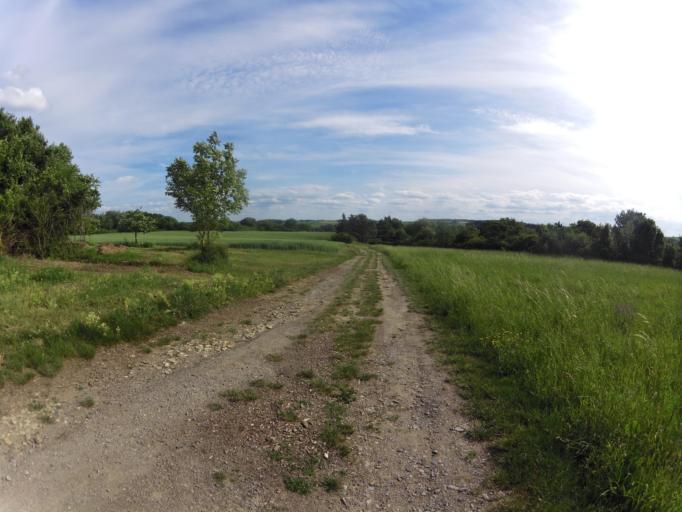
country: DE
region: Bavaria
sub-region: Regierungsbezirk Unterfranken
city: Ochsenfurt
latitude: 49.6741
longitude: 10.0671
